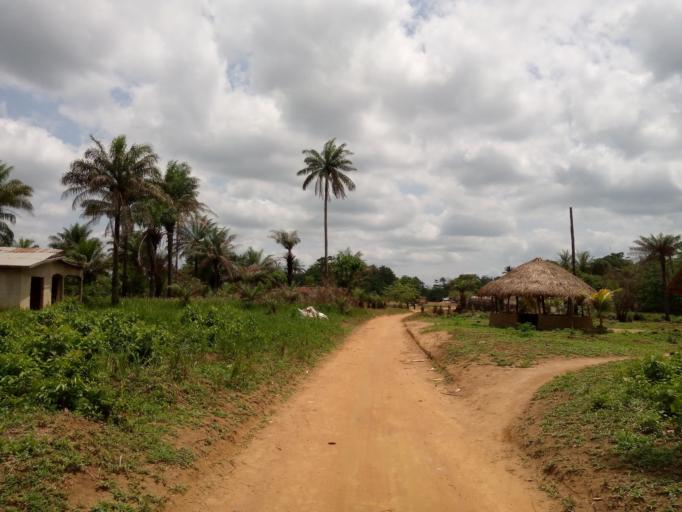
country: SL
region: Western Area
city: Waterloo
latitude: 8.4015
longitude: -12.9490
